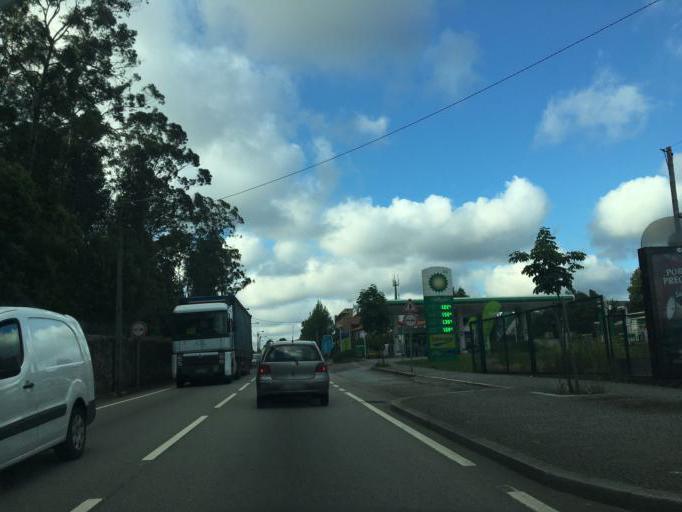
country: PT
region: Porto
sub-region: Maia
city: Anta
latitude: 41.2749
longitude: -8.6083
